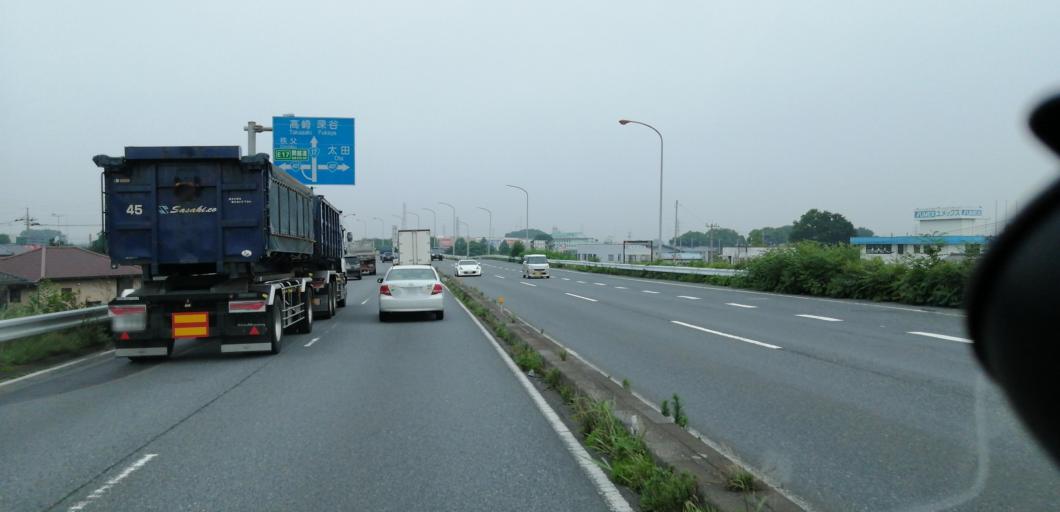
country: JP
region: Saitama
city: Kumagaya
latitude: 36.1712
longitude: 139.3753
